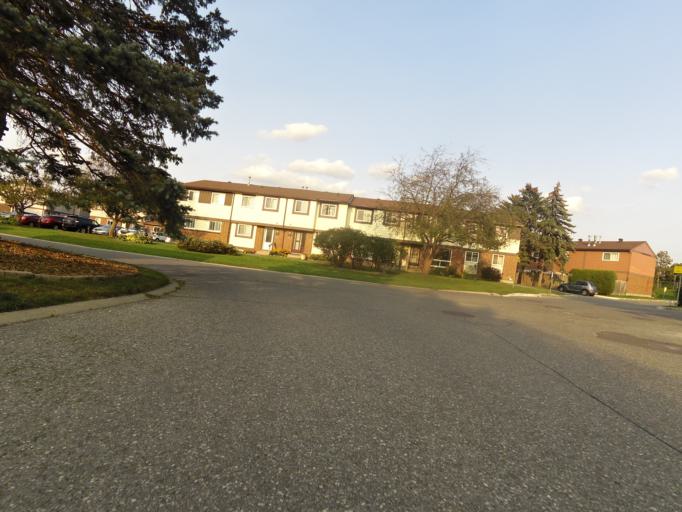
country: CA
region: Ontario
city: Bells Corners
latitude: 45.2836
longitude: -75.7504
